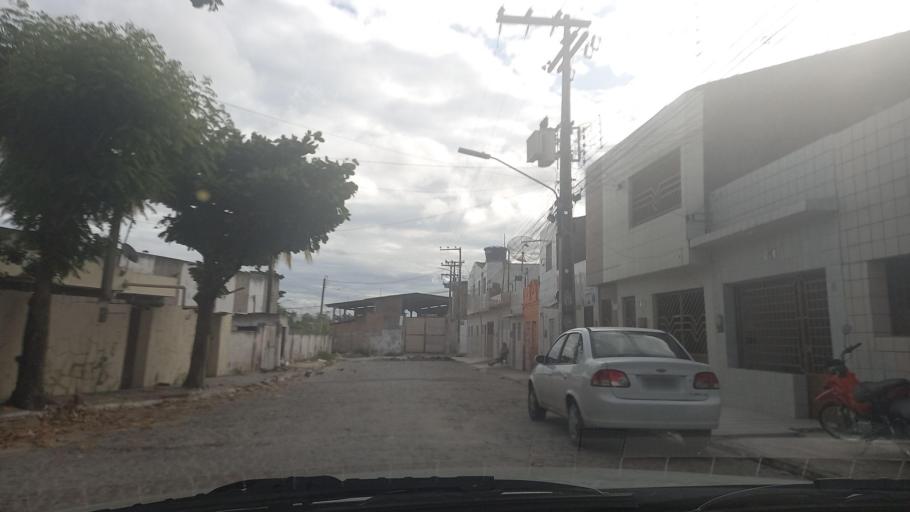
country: BR
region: Pernambuco
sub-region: Caruaru
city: Caruaru
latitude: -8.2917
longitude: -35.9799
